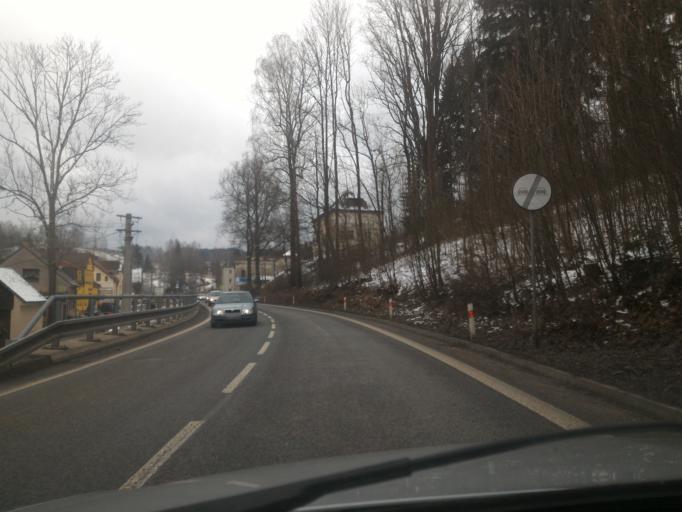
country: CZ
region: Liberecky
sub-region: Okres Jablonec nad Nisou
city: Lucany nad Nisou
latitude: 50.7385
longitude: 15.2100
